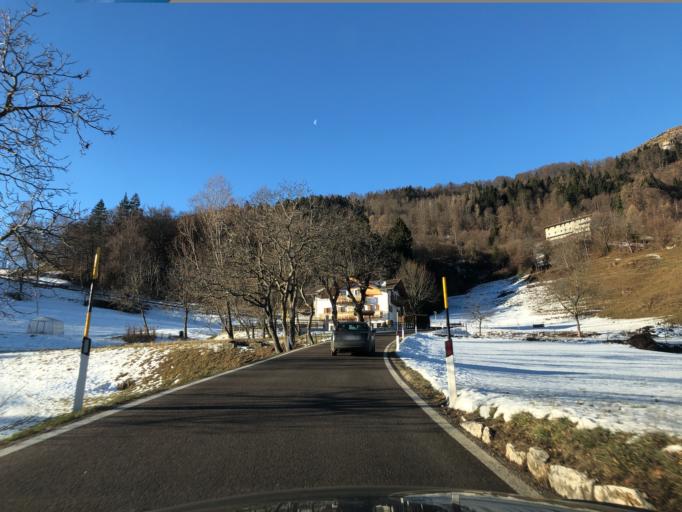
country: IT
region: Trentino-Alto Adige
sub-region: Provincia di Trento
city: Brentonico
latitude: 45.8081
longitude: 10.9402
